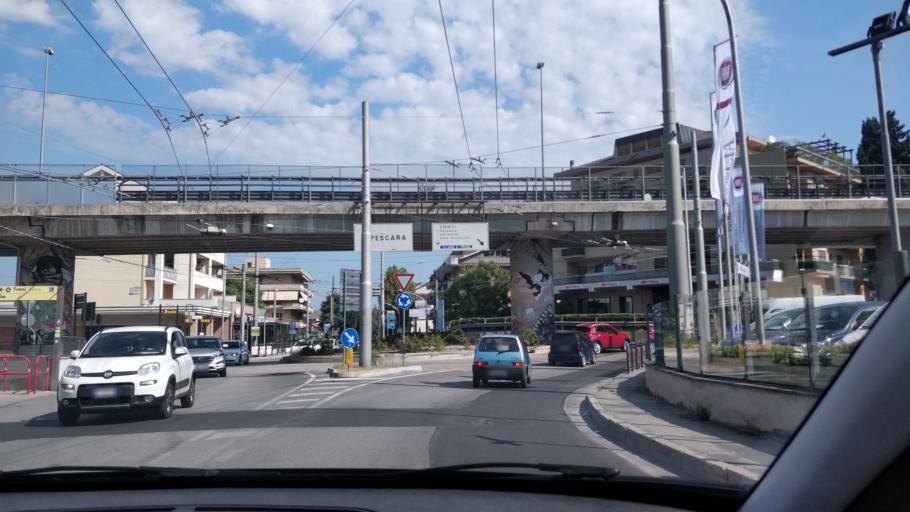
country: IT
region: Abruzzo
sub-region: Provincia di Chieti
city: Chieti
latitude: 42.3722
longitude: 14.1435
